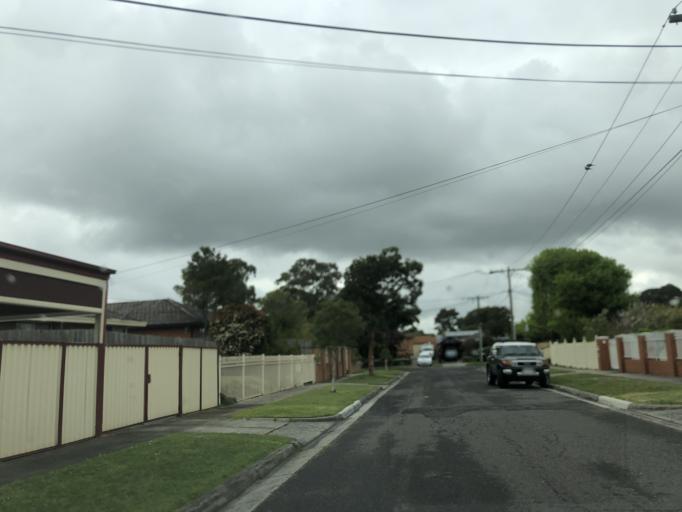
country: AU
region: Victoria
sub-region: Greater Dandenong
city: Dandenong North
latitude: -37.9594
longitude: 145.2151
